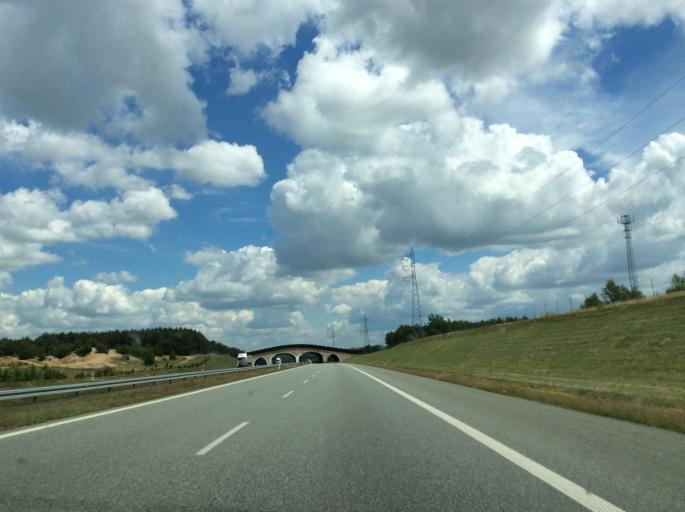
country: PL
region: Greater Poland Voivodeship
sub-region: Powiat turecki
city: Tuliszkow
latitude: 52.1403
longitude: 18.3470
